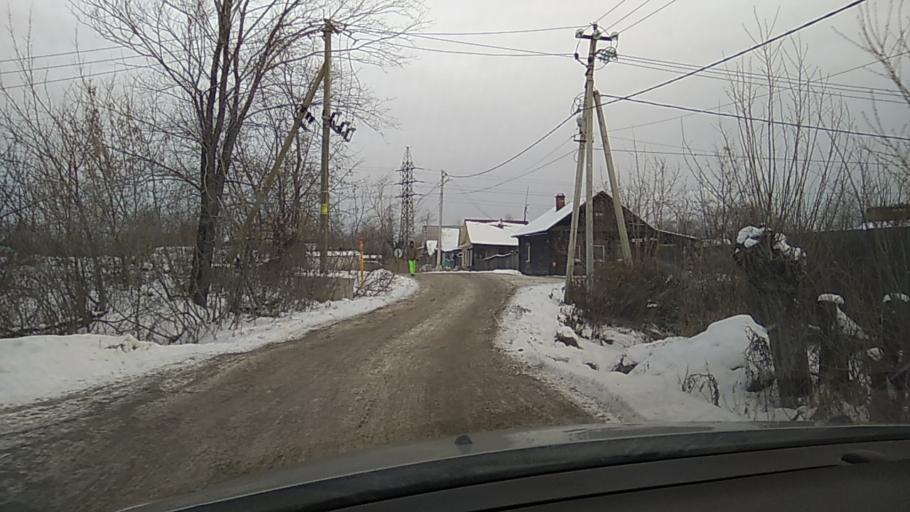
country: RU
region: Sverdlovsk
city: Shirokaya Rechka
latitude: 56.8341
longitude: 60.5281
